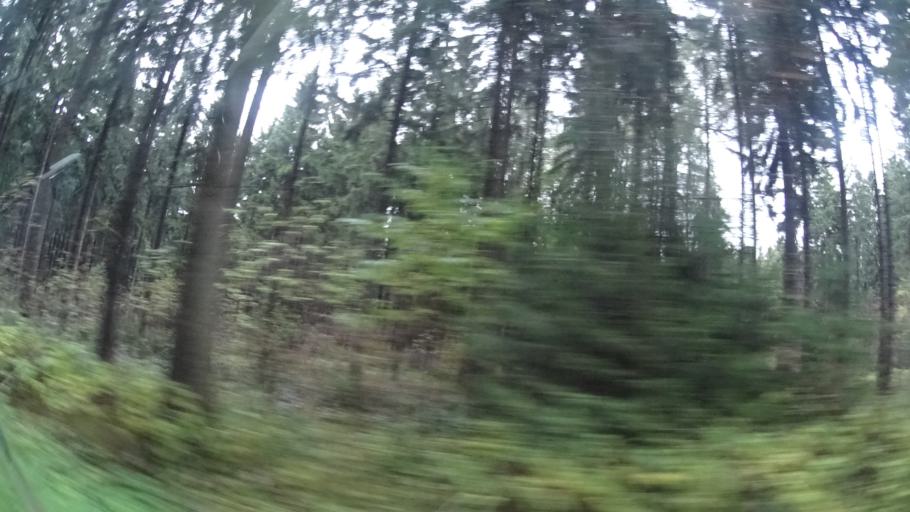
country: DE
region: Thuringia
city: Wurzbach
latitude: 50.4342
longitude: 11.4941
